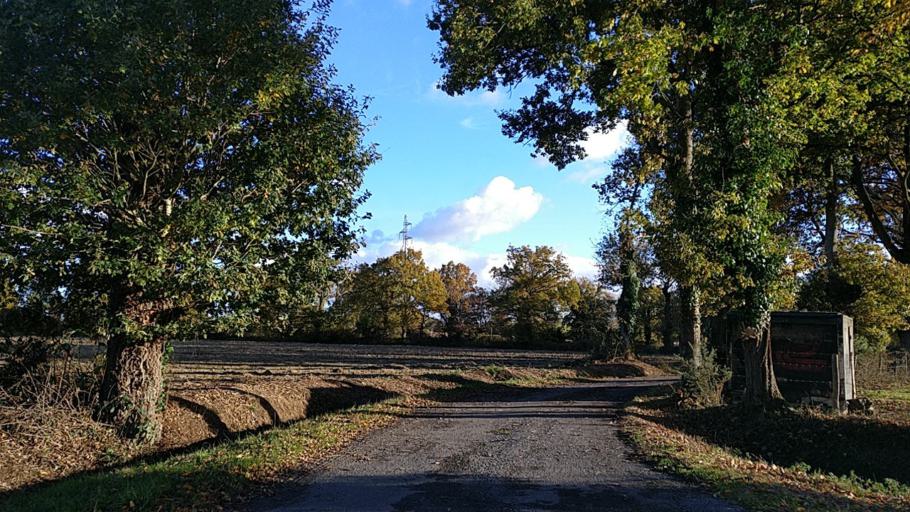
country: FR
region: Brittany
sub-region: Departement d'Ille-et-Vilaine
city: Fouillard
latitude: 48.1306
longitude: -1.5673
